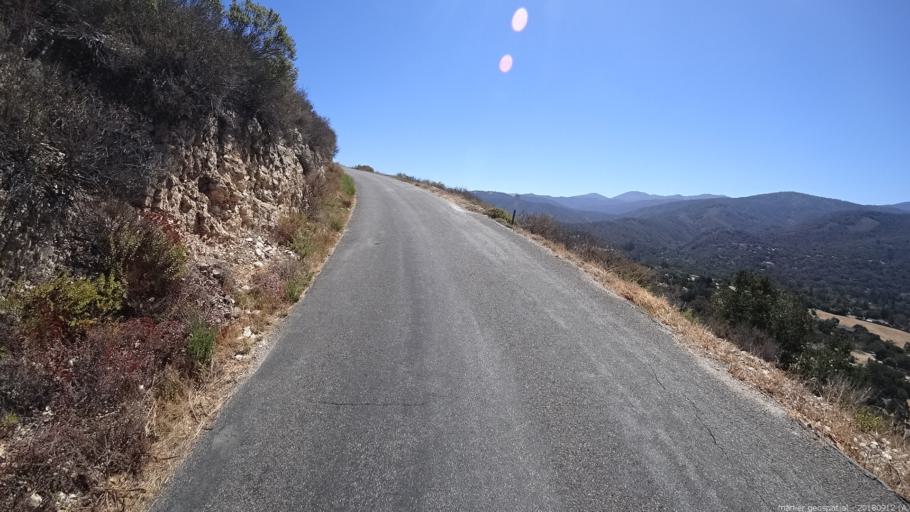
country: US
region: California
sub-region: Monterey County
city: Carmel Valley Village
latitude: 36.4842
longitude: -121.7234
